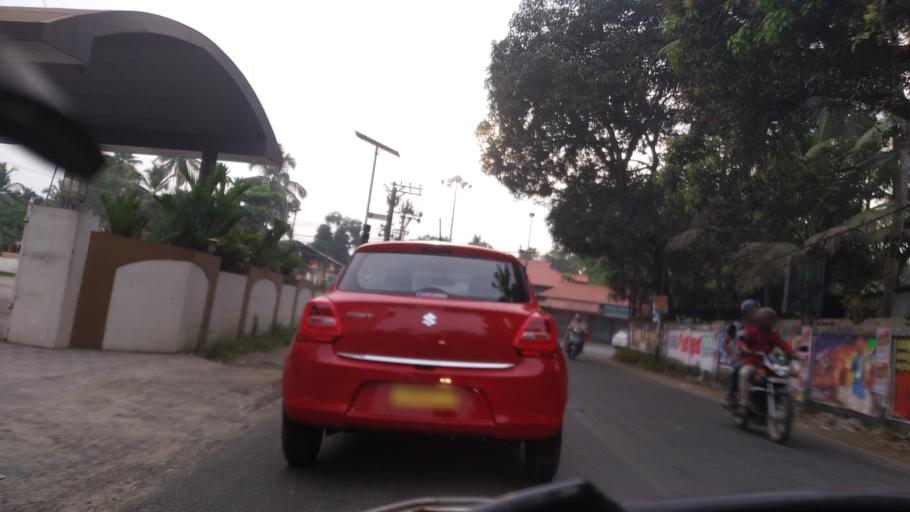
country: IN
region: Kerala
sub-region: Thrissur District
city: Kodungallur
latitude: 10.1403
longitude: 76.2300
